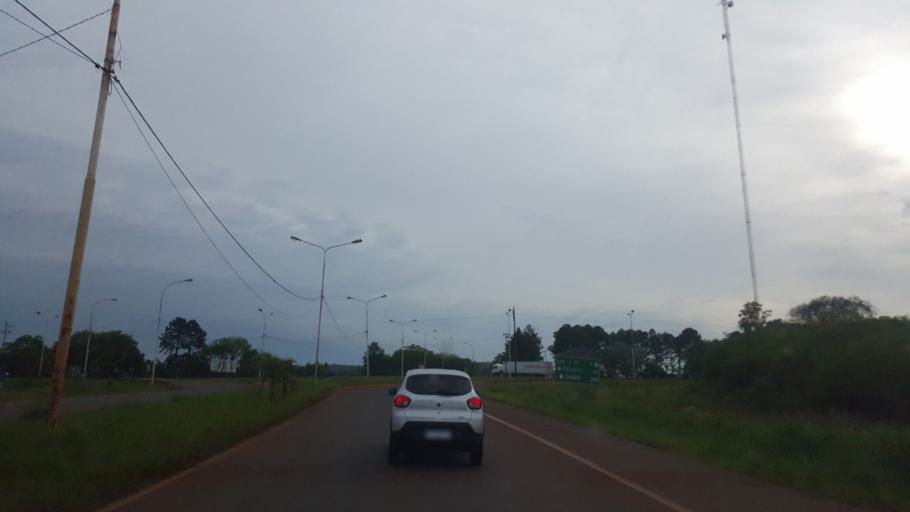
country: AR
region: Misiones
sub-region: Departamento de Apostoles
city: San Jose
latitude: -27.7472
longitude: -55.7822
